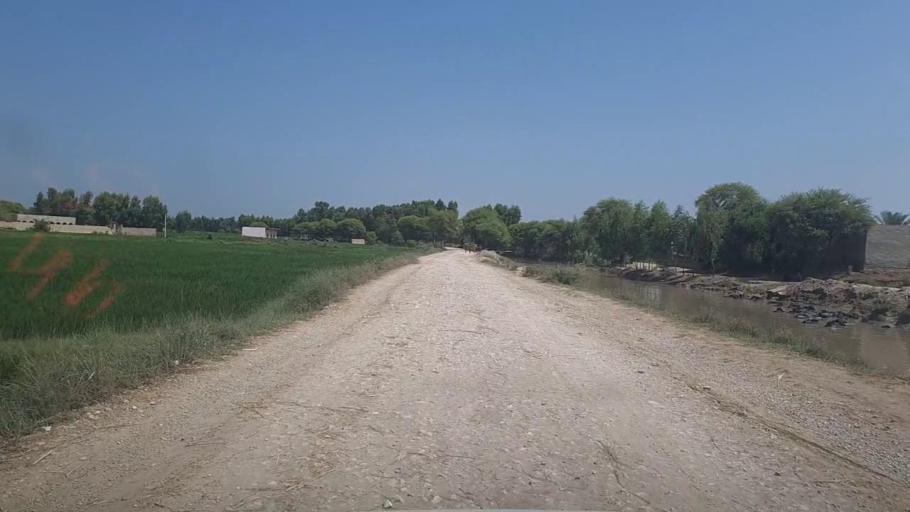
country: PK
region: Sindh
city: Kandhkot
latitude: 28.2709
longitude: 69.2265
